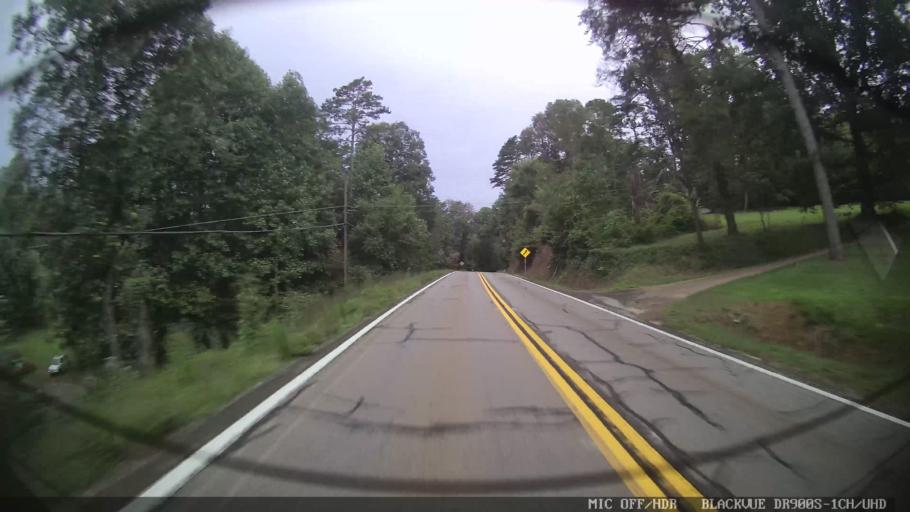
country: US
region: Georgia
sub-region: Gilmer County
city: Ellijay
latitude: 34.7084
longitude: -84.4954
